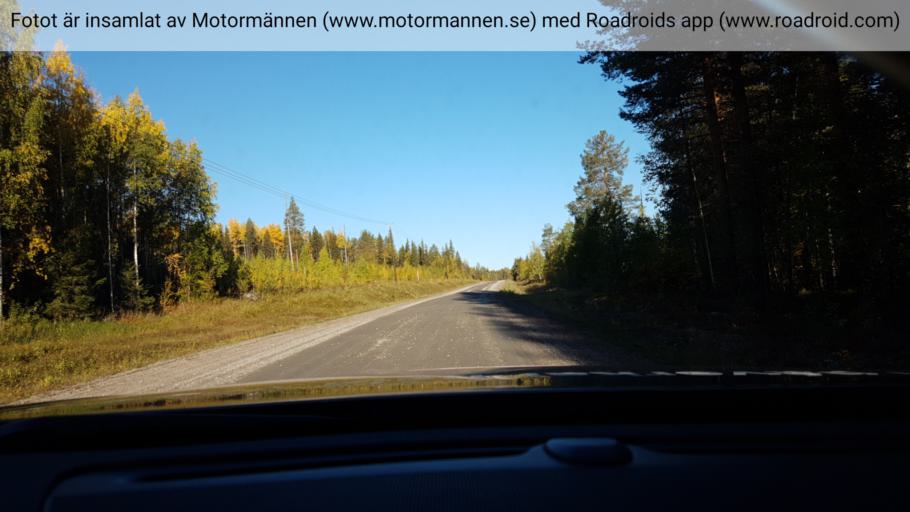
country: SE
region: Norrbotten
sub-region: Bodens Kommun
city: Boden
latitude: 66.1571
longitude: 21.2603
